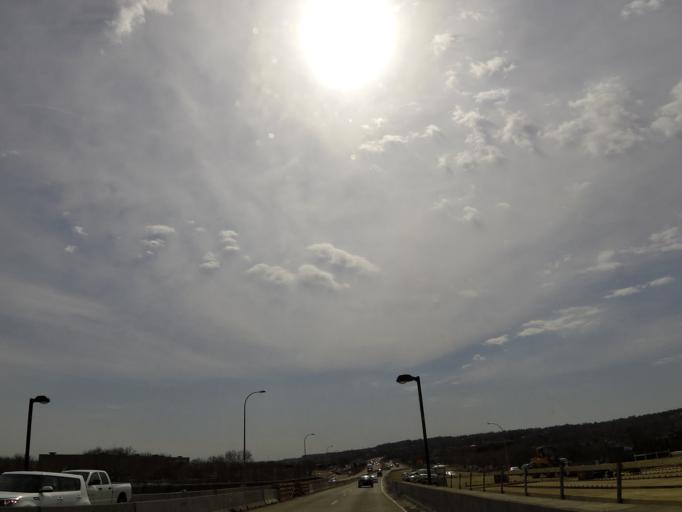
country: US
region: Minnesota
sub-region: Ramsey County
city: Saint Paul
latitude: 44.9442
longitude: -93.0777
